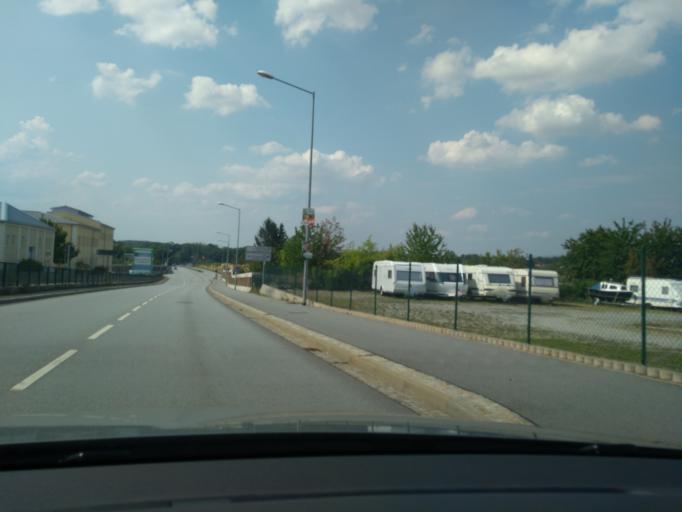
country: DE
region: Saxony
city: Bautzen
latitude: 51.1690
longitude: 14.4211
